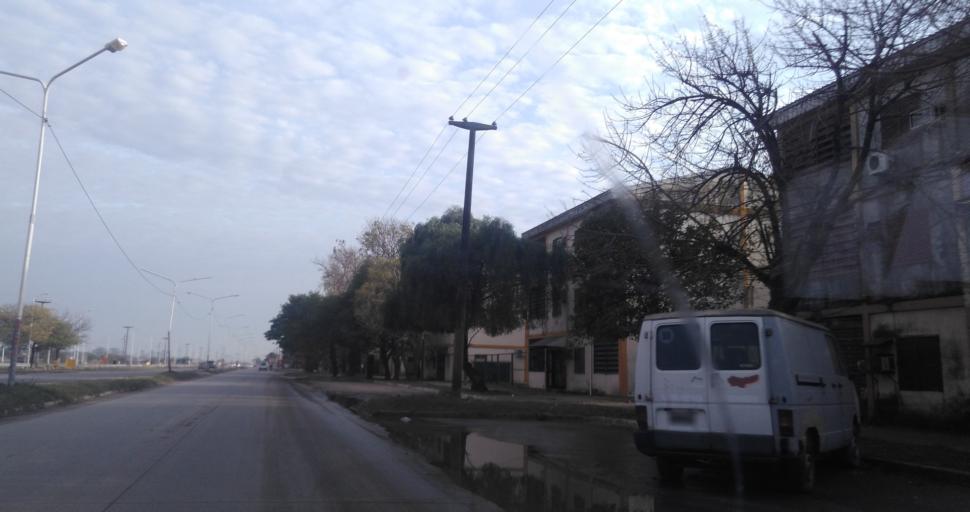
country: AR
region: Chaco
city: Resistencia
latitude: -27.4694
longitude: -59.0089
